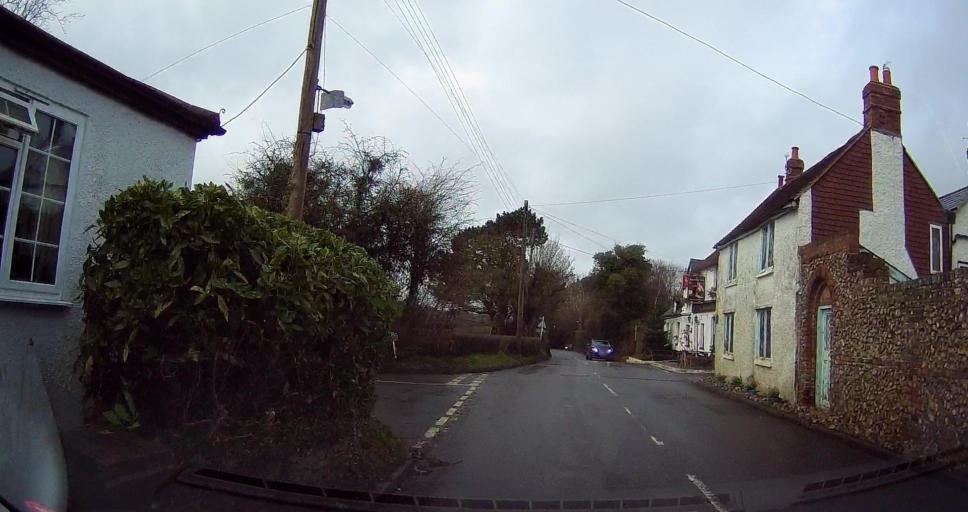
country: GB
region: England
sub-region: Kent
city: Biggin Hill
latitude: 51.3185
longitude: 0.0731
